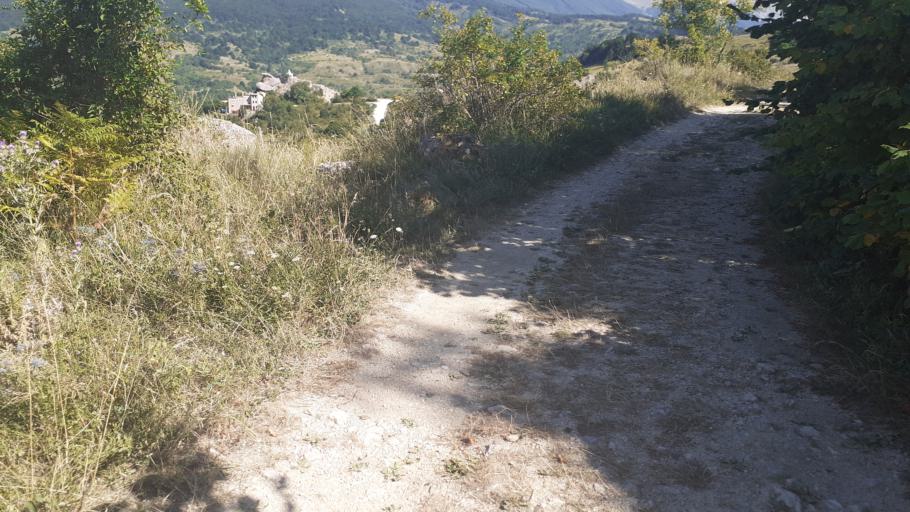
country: IT
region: Abruzzo
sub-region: Provincia di Pescara
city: Sant'Eufemia a Maiella
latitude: 42.1040
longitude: 14.0085
